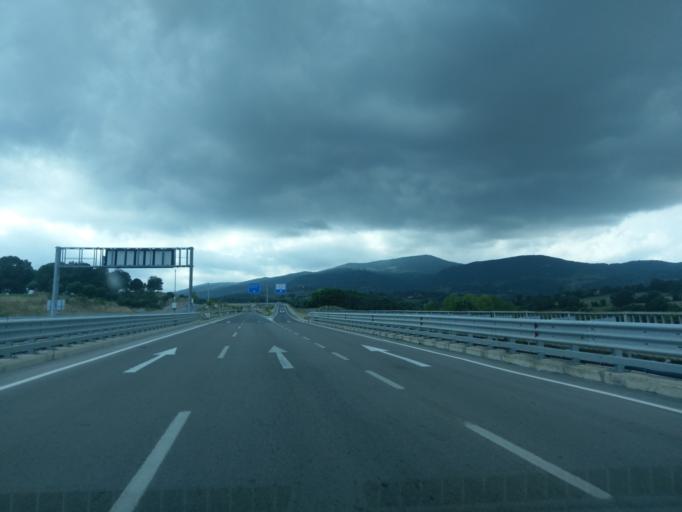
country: TR
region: Sinop
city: Gerze
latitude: 41.8165
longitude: 35.1676
